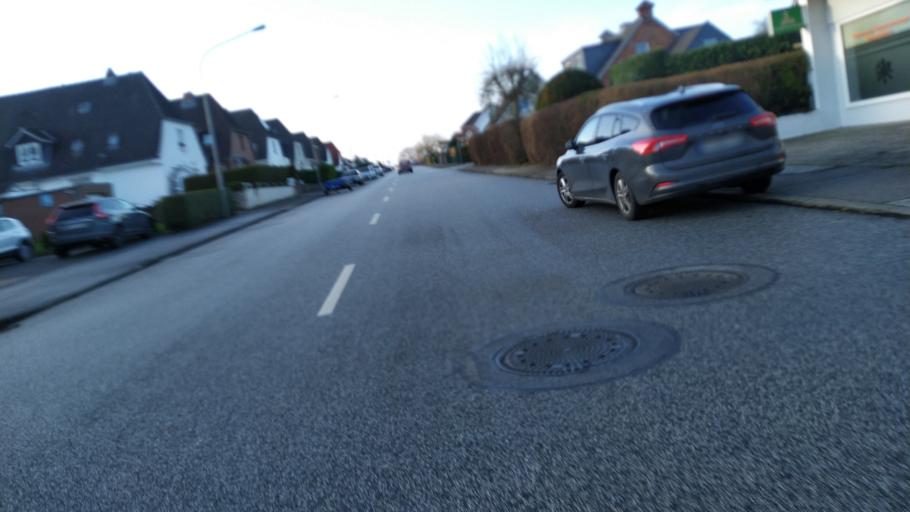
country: DE
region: Schleswig-Holstein
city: Travemuende
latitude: 53.9578
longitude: 10.8536
